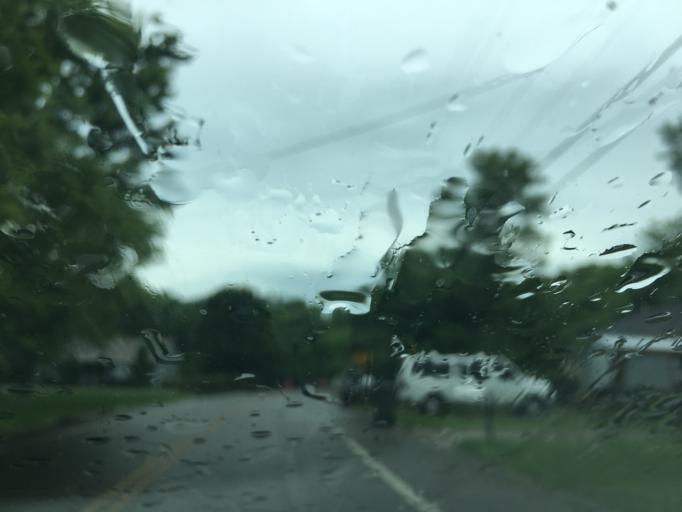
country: US
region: Tennessee
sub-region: Davidson County
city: Belle Meade
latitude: 36.0529
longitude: -86.9453
